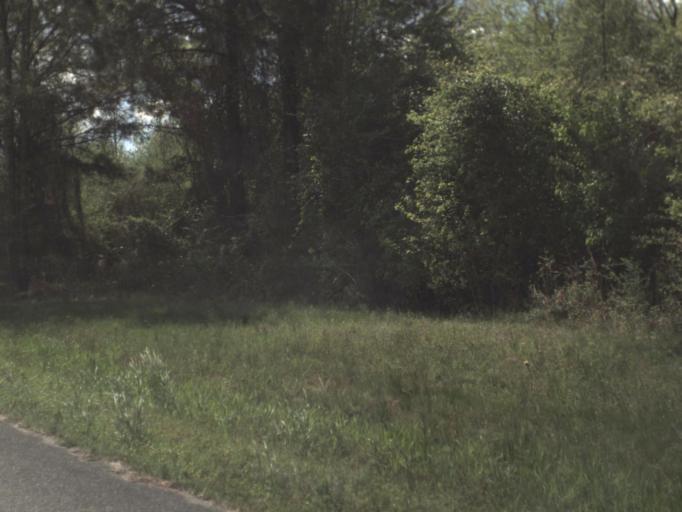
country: US
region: Florida
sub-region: Okaloosa County
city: Crestview
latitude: 30.9461
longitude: -86.6341
